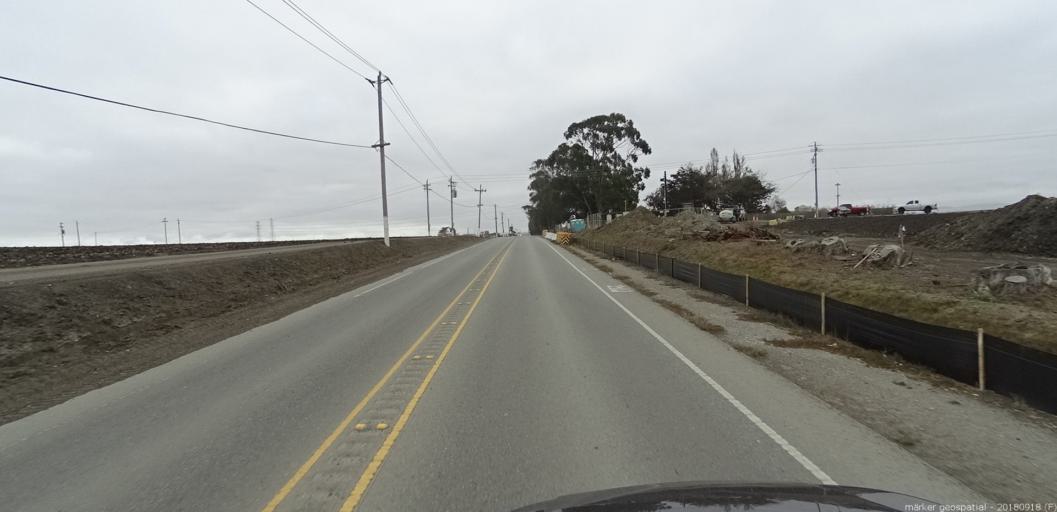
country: US
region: California
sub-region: Monterey County
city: Castroville
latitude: 36.7443
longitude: -121.7292
